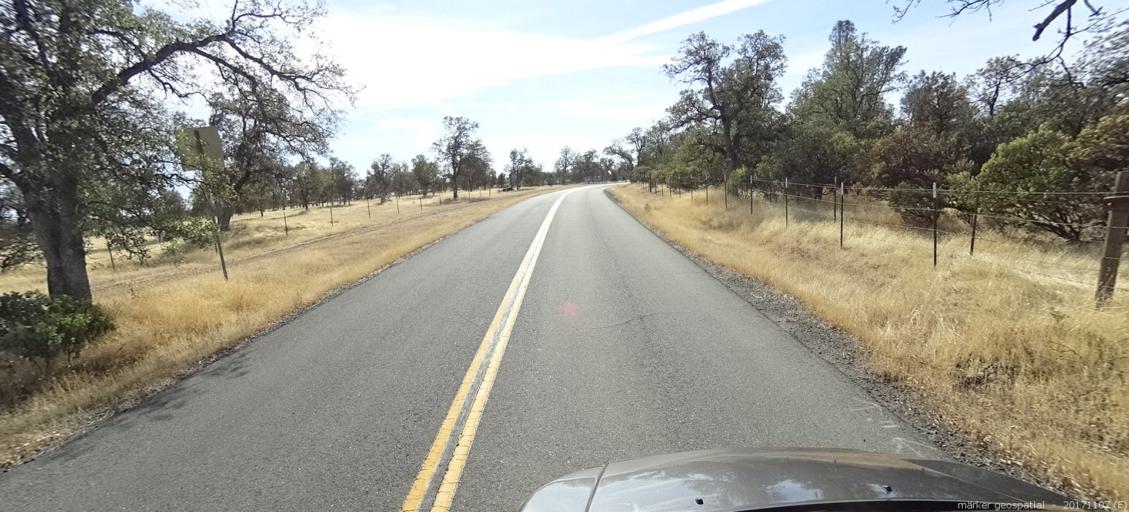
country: US
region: California
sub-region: Shasta County
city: Shasta
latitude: 40.4750
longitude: -122.5442
